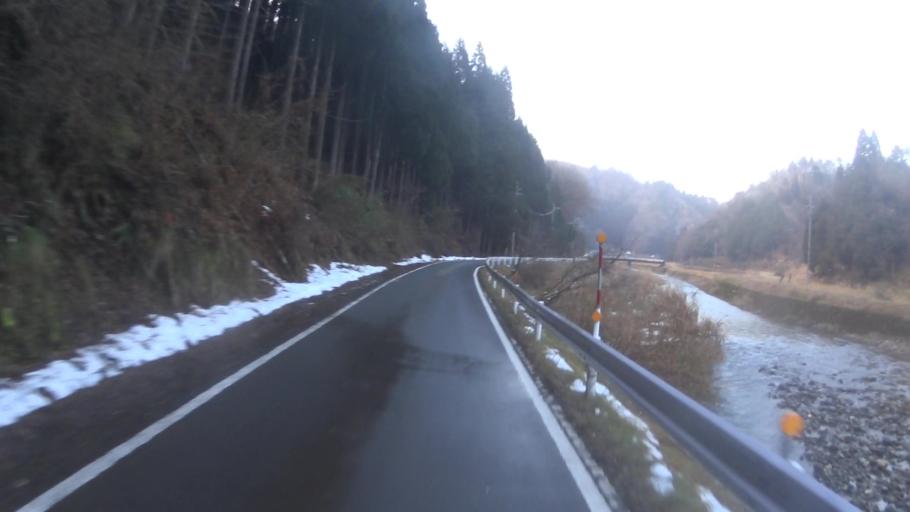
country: JP
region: Kyoto
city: Maizuru
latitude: 35.3881
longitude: 135.4734
